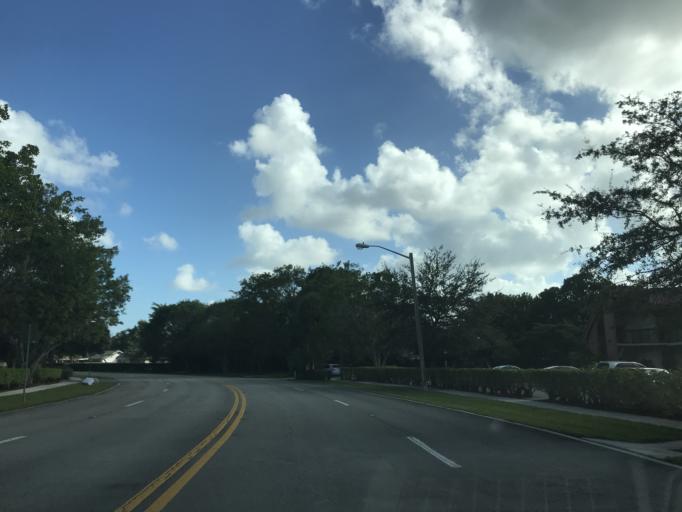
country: US
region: Florida
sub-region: Broward County
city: Coconut Creek
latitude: 26.2494
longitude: -80.1918
